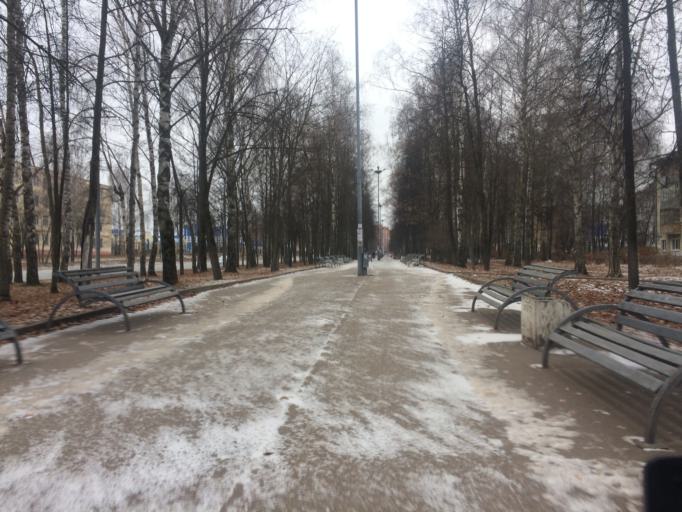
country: RU
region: Mariy-El
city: Yoshkar-Ola
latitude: 56.6441
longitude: 47.8735
